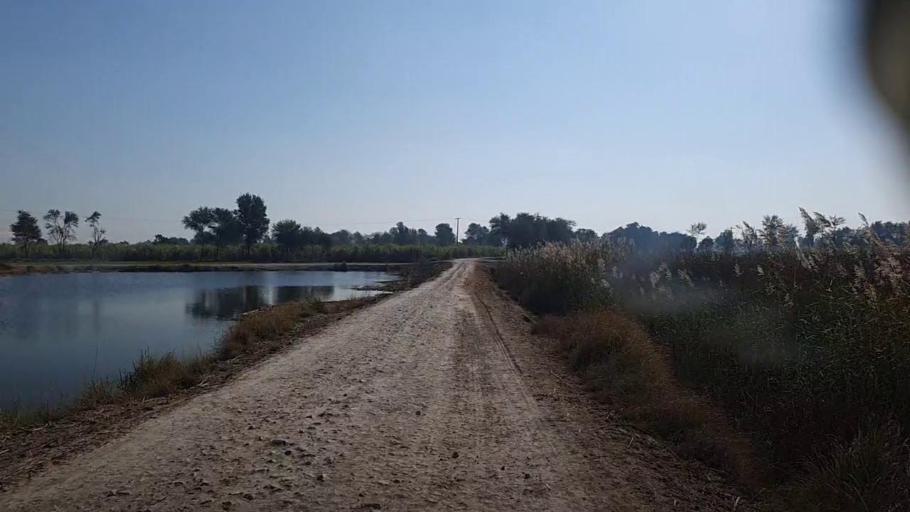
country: PK
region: Sindh
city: Khairpur
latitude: 28.0592
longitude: 69.7454
